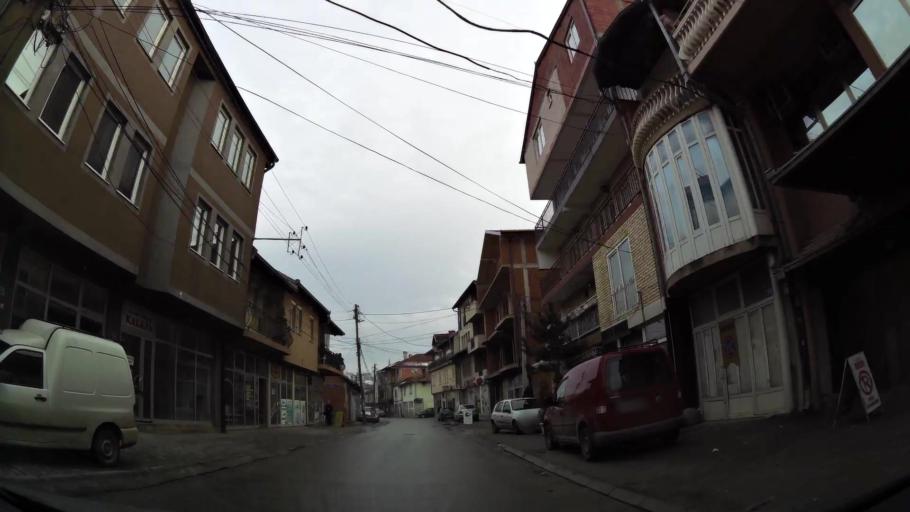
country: XK
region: Pristina
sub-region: Komuna e Prishtines
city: Pristina
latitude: 42.6722
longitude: 21.1670
